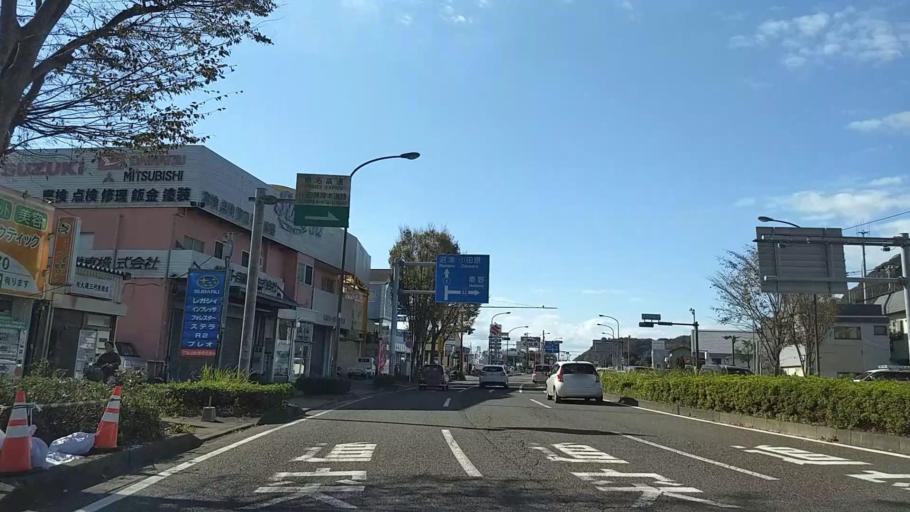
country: JP
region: Kanagawa
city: Hiratsuka
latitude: 35.3249
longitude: 139.3315
